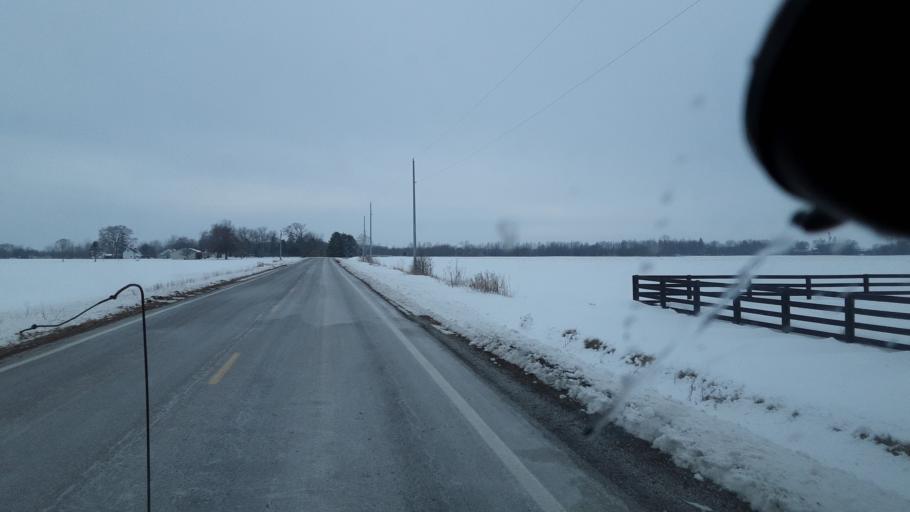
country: US
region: Ohio
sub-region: Champaign County
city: Mechanicsburg
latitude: 40.1206
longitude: -83.4458
